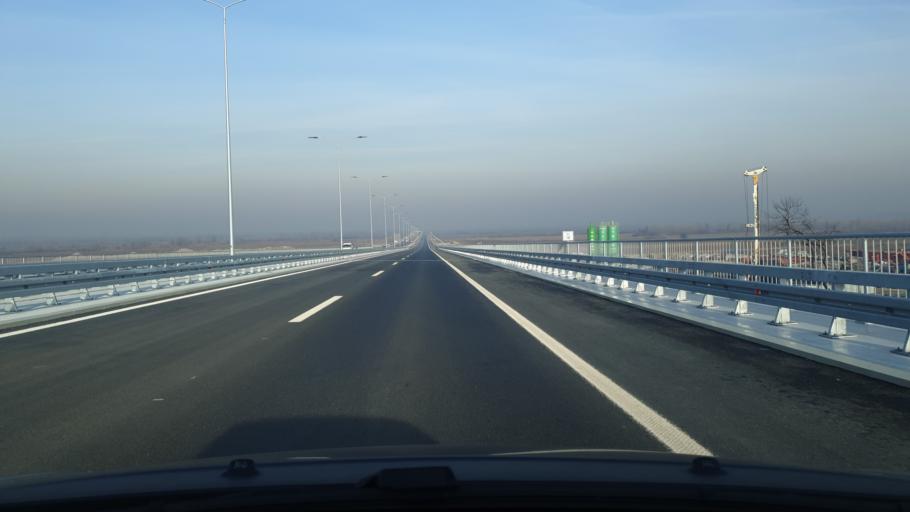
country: RS
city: Baric
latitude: 44.6689
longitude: 20.2493
